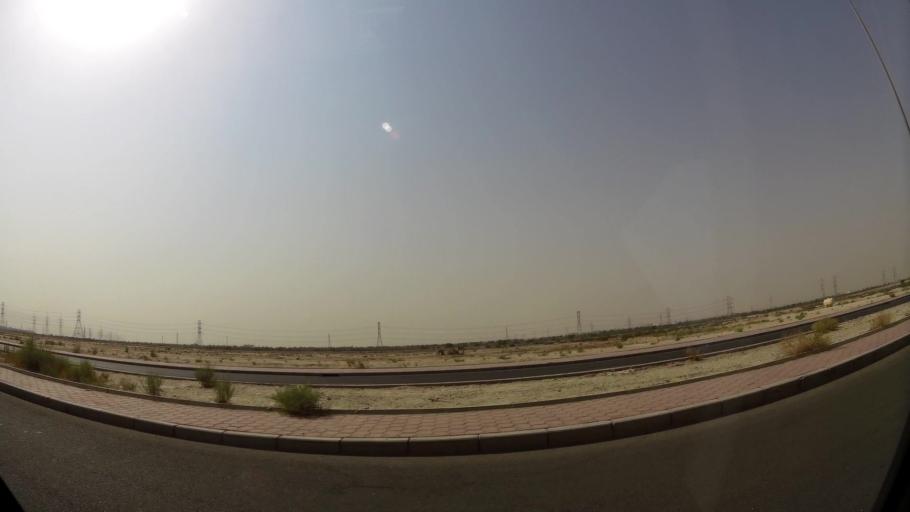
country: KW
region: Muhafazat al Jahra'
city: Al Jahra'
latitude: 29.3247
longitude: 47.7752
